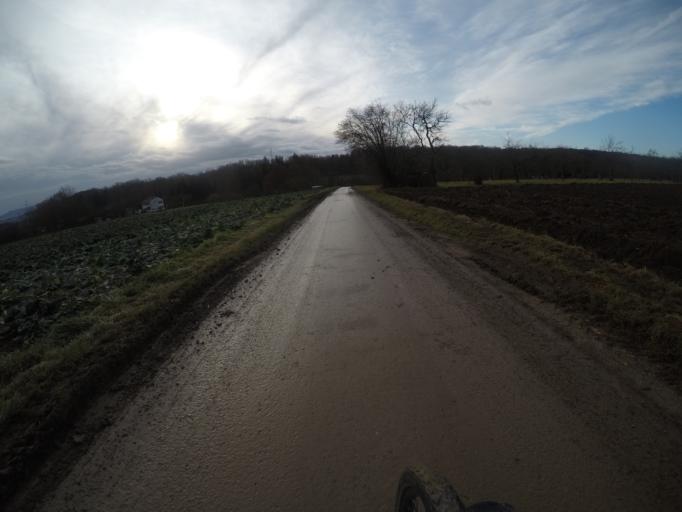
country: DE
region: Baden-Wuerttemberg
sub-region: Regierungsbezirk Stuttgart
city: Kongen
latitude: 48.6764
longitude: 9.3387
